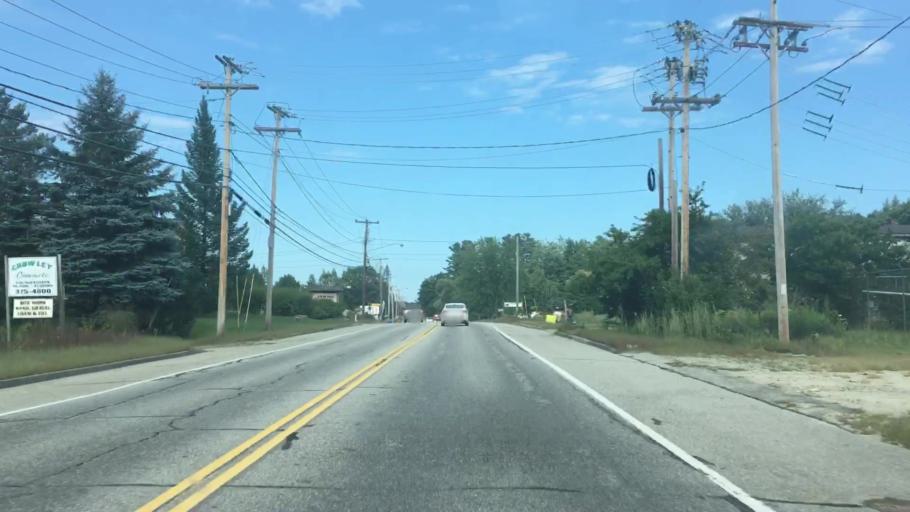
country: US
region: Maine
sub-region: Androscoggin County
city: Sabattus
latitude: 44.1018
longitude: -70.1407
